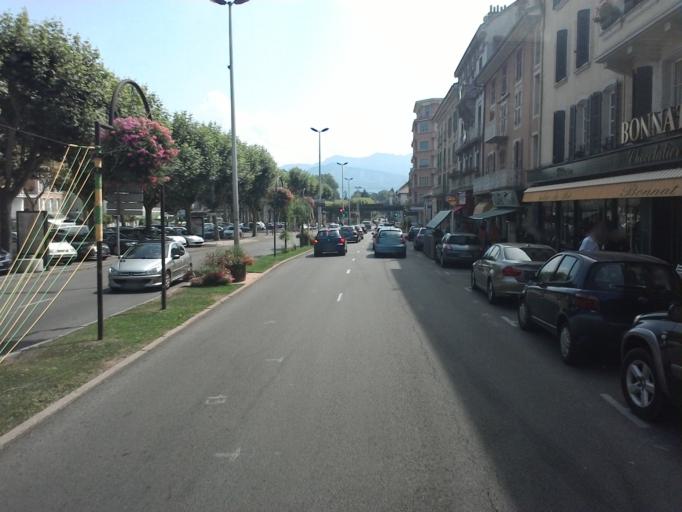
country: FR
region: Rhone-Alpes
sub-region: Departement de l'Isere
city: Voiron
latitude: 45.3668
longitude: 5.5911
